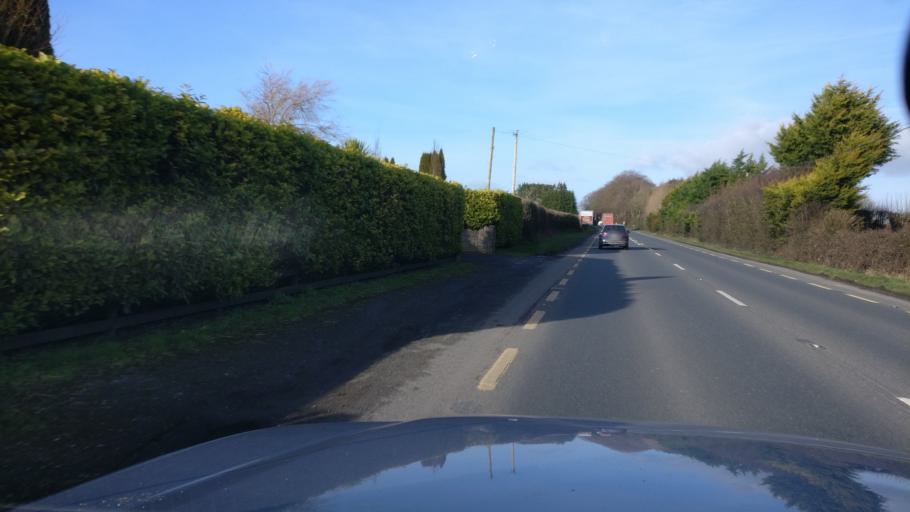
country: IE
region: Leinster
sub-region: Uibh Fhaili
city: Tullamore
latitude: 53.2493
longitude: -7.4773
